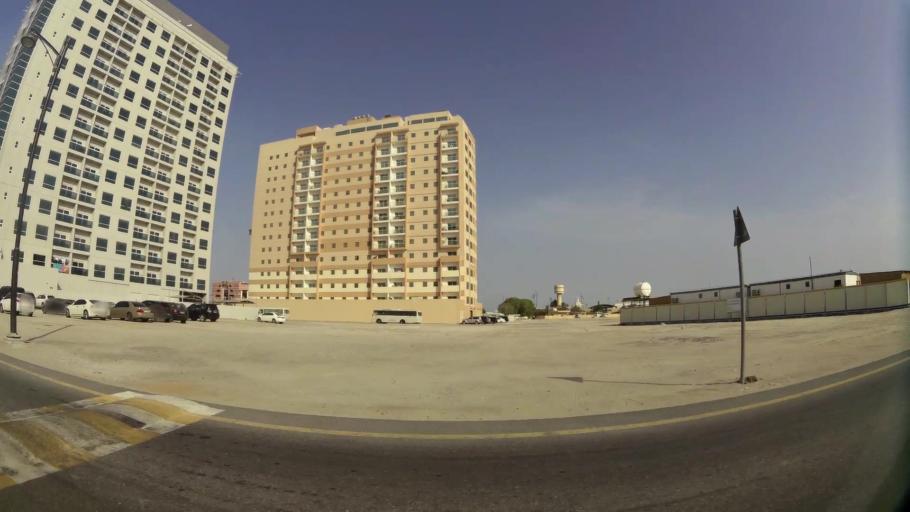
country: AE
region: Ash Shariqah
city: Sharjah
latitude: 25.2847
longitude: 55.3561
